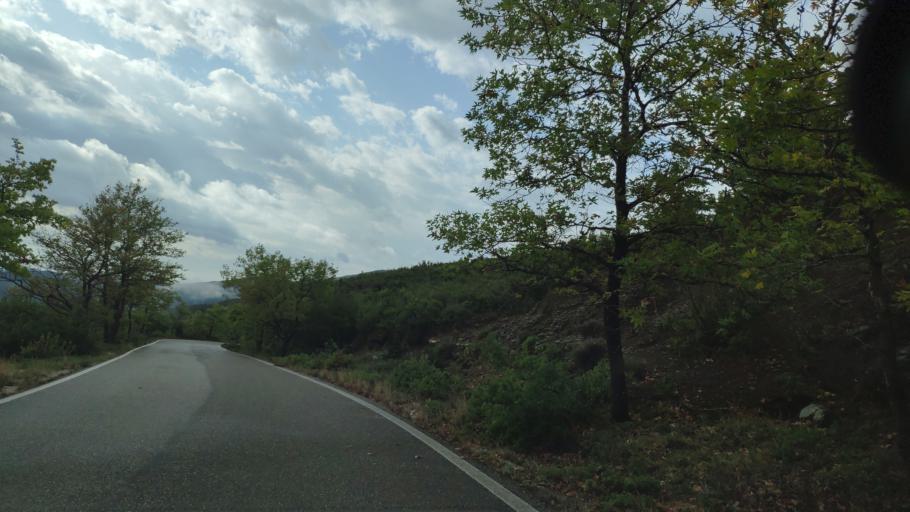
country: GR
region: West Greece
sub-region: Nomos Aitolias kai Akarnanias
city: Sardinia
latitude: 38.8448
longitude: 21.3168
